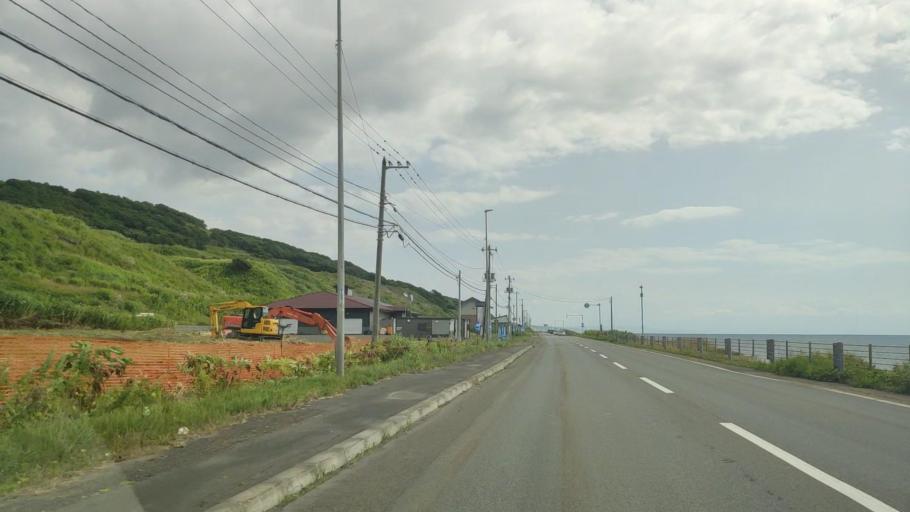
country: JP
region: Hokkaido
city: Rumoi
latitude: 44.1346
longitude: 141.6550
